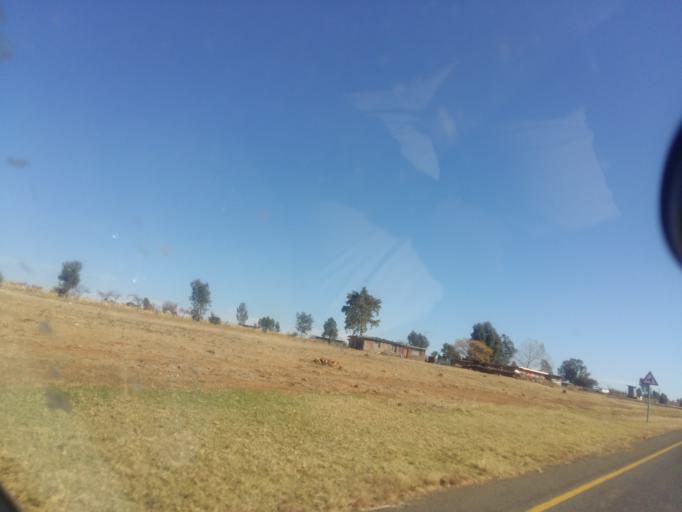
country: LS
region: Mafeteng
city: Mafeteng
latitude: -29.6638
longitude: 27.2710
